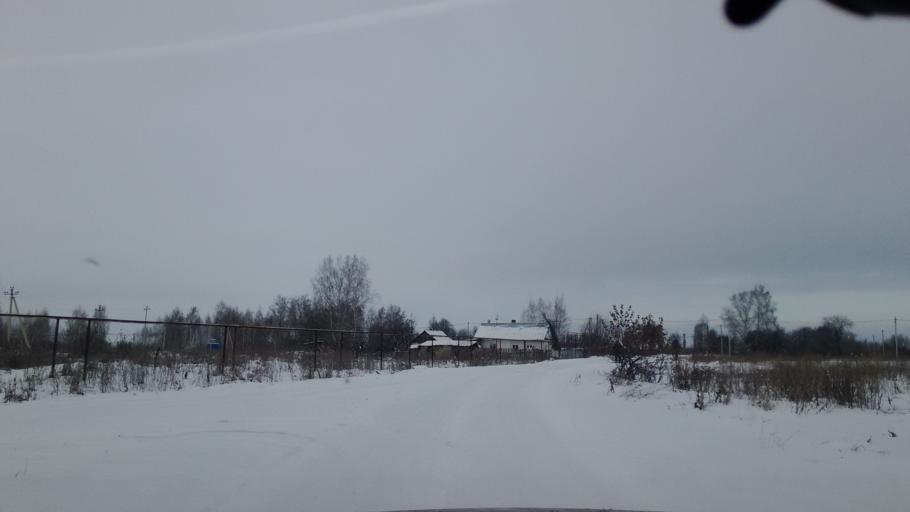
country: RU
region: Tula
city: Bogoroditsk
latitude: 53.7512
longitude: 38.1063
